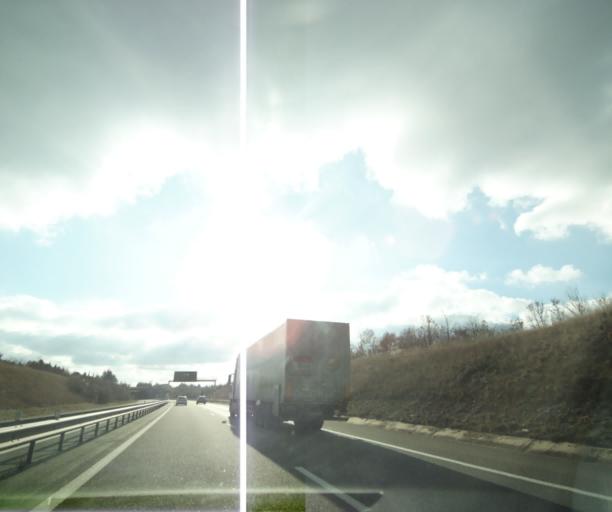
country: FR
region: Midi-Pyrenees
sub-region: Departement du Lot
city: Cahors
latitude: 44.5051
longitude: 1.4971
